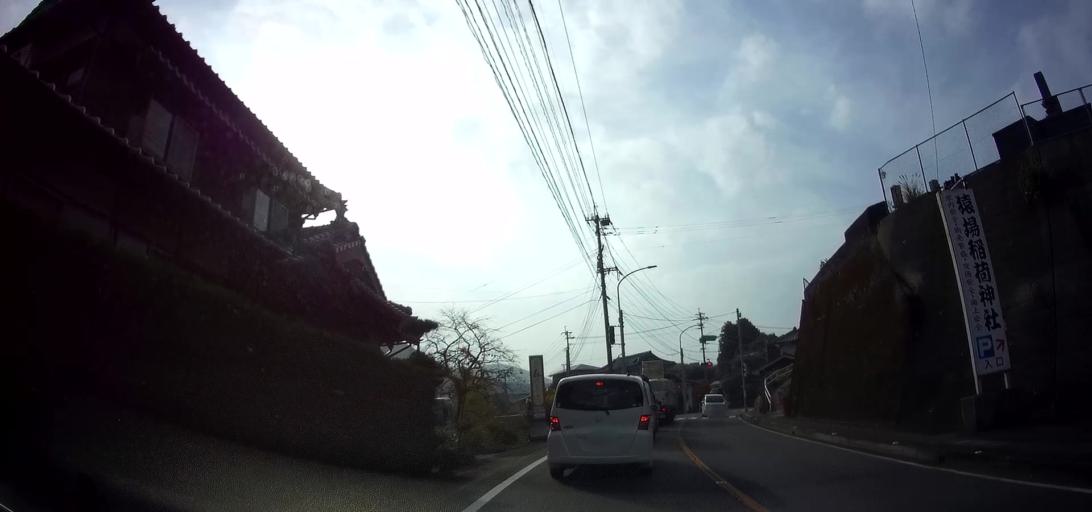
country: JP
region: Nagasaki
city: Shimabara
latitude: 32.7666
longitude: 130.2141
